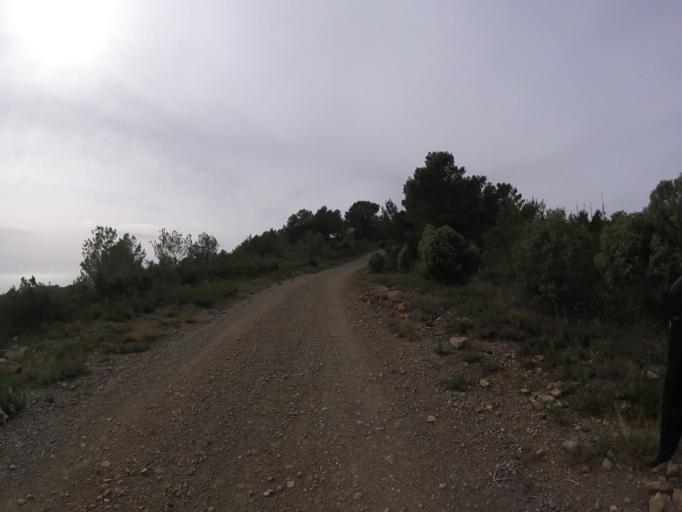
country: ES
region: Valencia
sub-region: Provincia de Castello
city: Benicassim
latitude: 40.0904
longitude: 0.0378
